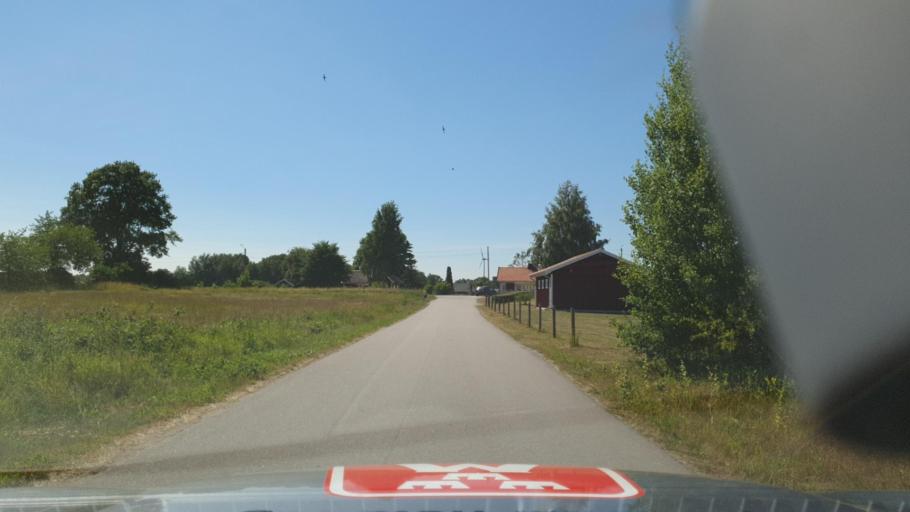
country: SE
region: Kalmar
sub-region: Torsas Kommun
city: Torsas
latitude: 56.3646
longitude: 16.0679
